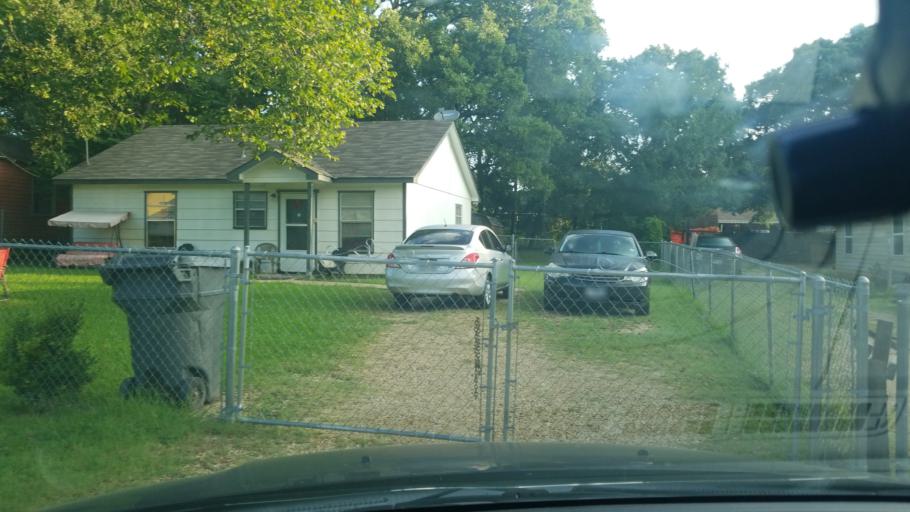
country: US
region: Texas
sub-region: Dallas County
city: Balch Springs
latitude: 32.7247
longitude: -96.6541
